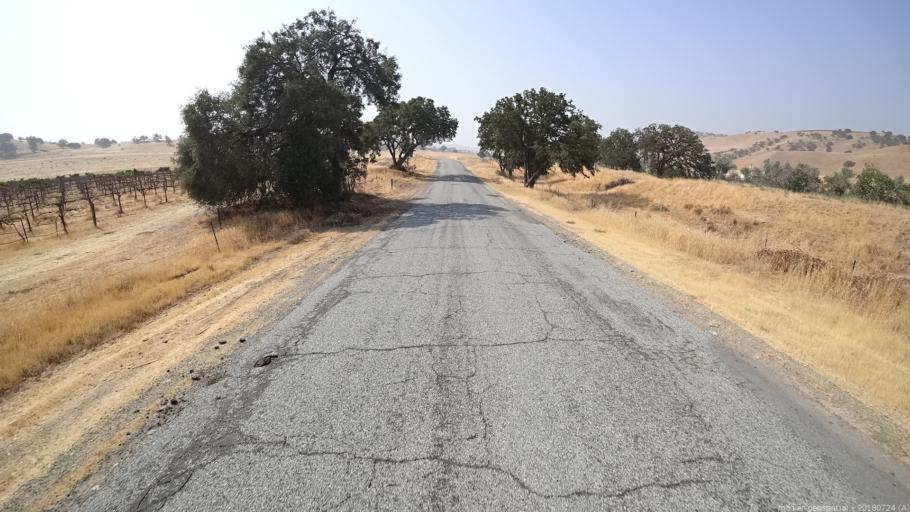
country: US
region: California
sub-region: San Luis Obispo County
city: San Miguel
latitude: 35.8425
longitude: -120.7005
